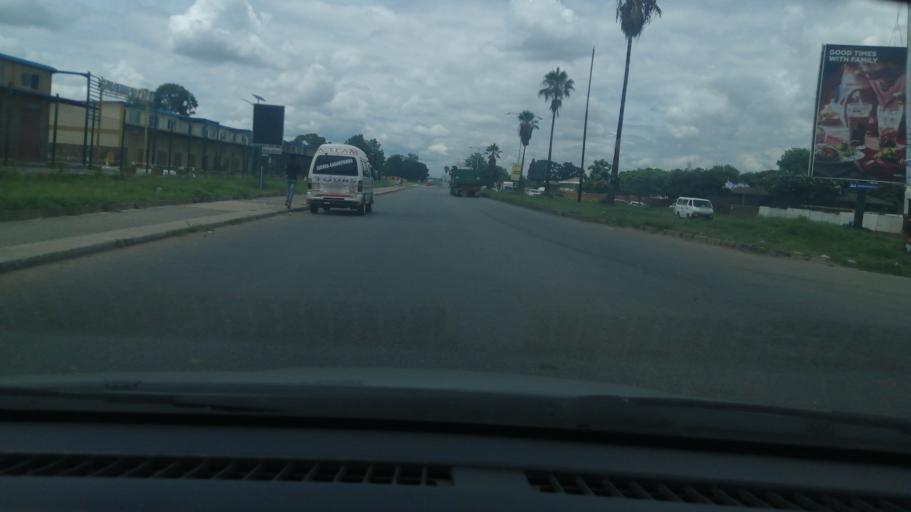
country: ZW
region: Harare
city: Harare
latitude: -17.8672
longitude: 31.0236
